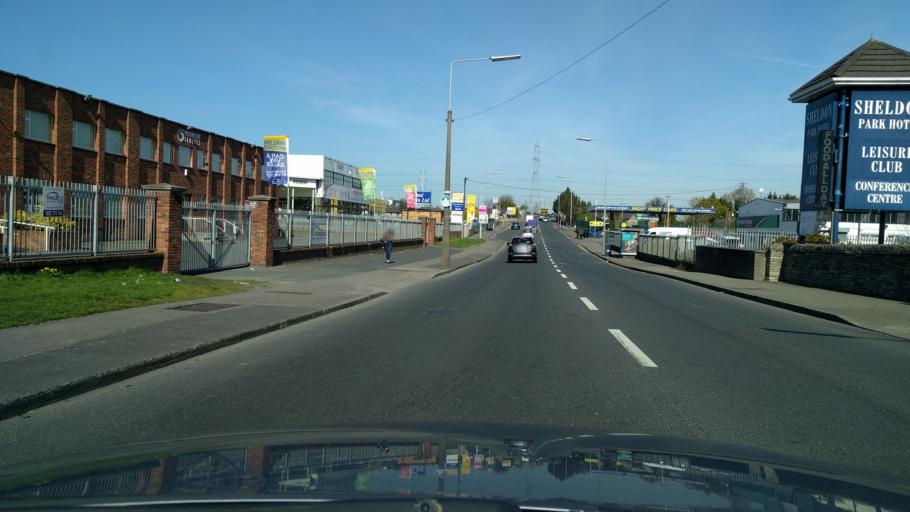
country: IE
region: Leinster
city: Crumlin
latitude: 53.3295
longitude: -6.3448
